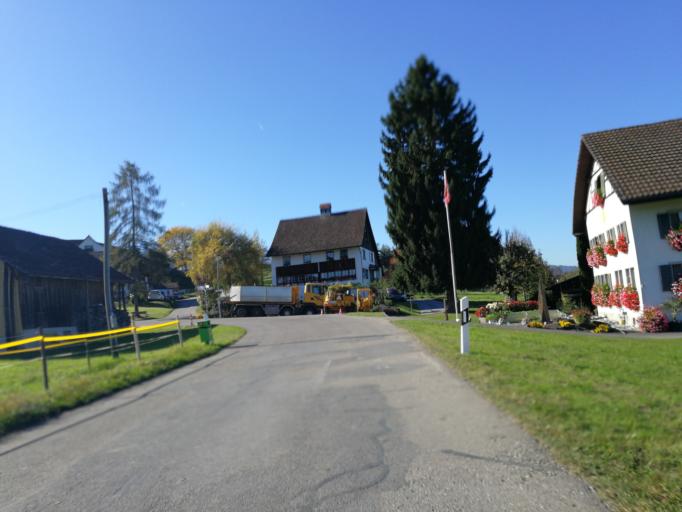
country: CH
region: Zurich
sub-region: Bezirk Hinwil
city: Binzikon
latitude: 47.2652
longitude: 8.7548
